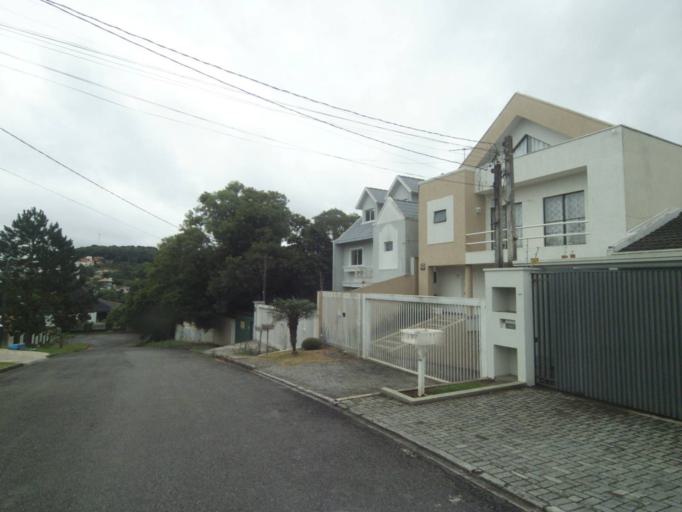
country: BR
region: Parana
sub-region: Curitiba
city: Curitiba
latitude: -25.4268
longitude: -49.3226
